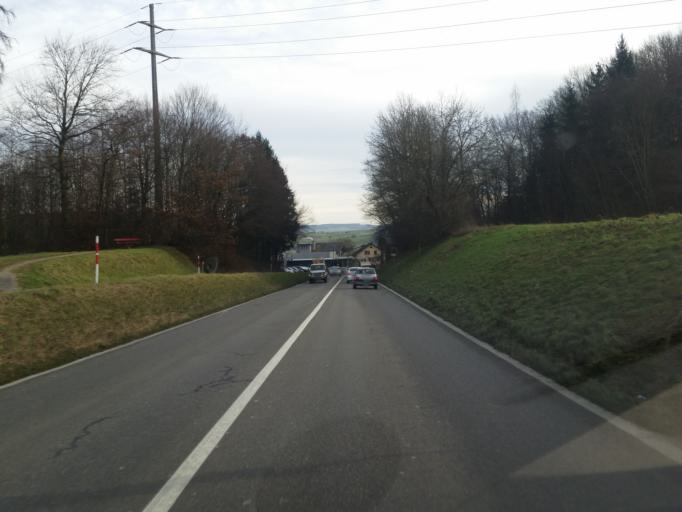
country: CH
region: Aargau
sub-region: Bezirk Lenzburg
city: Othmarsingen
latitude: 47.3894
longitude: 8.2002
